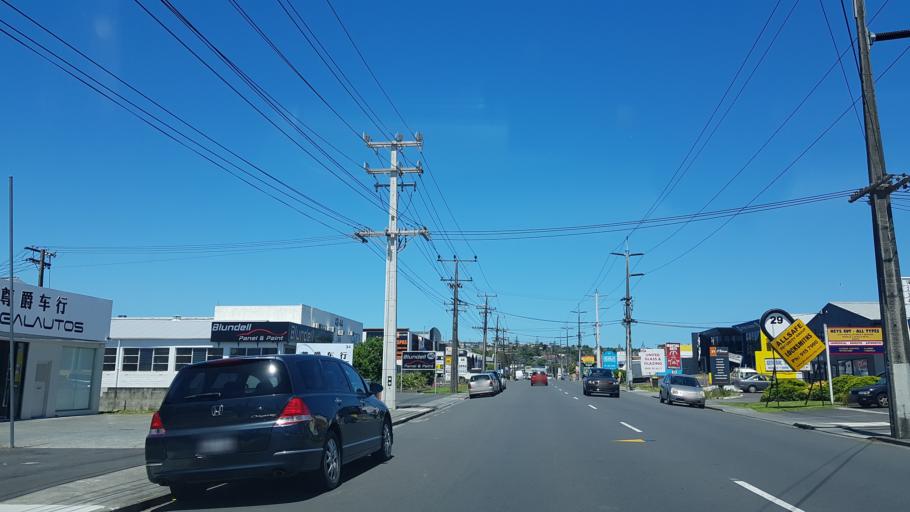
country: NZ
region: Auckland
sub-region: Auckland
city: North Shore
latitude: -36.7818
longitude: 174.7425
